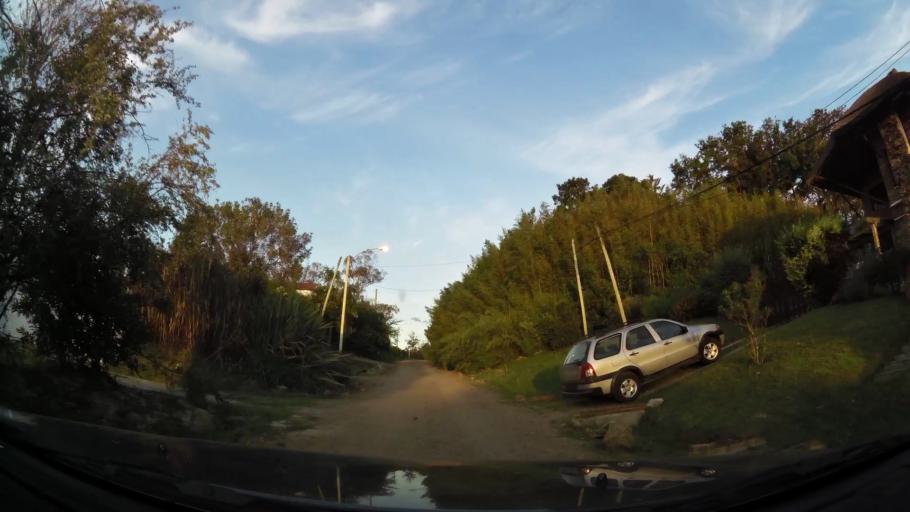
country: UY
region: Canelones
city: Atlantida
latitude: -34.7704
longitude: -55.7723
